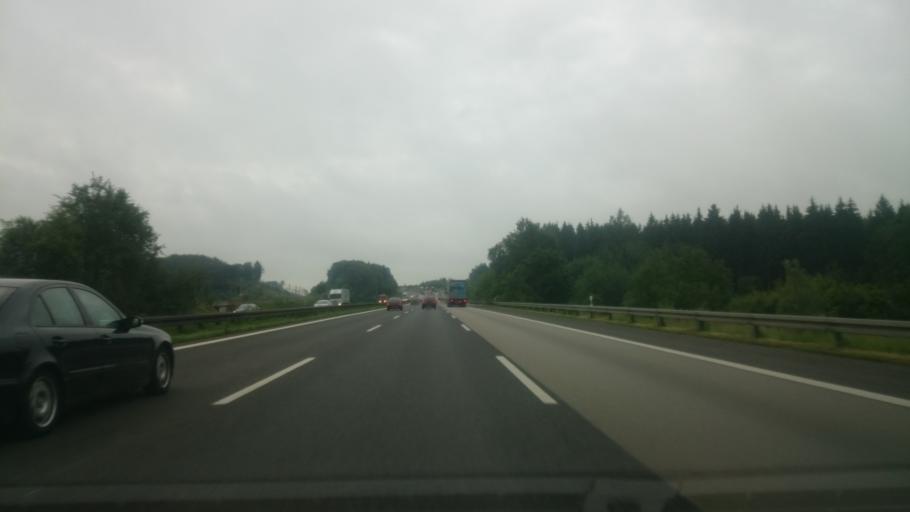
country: DE
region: Bavaria
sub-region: Upper Bavaria
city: Stammham
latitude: 48.8898
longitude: 11.4664
